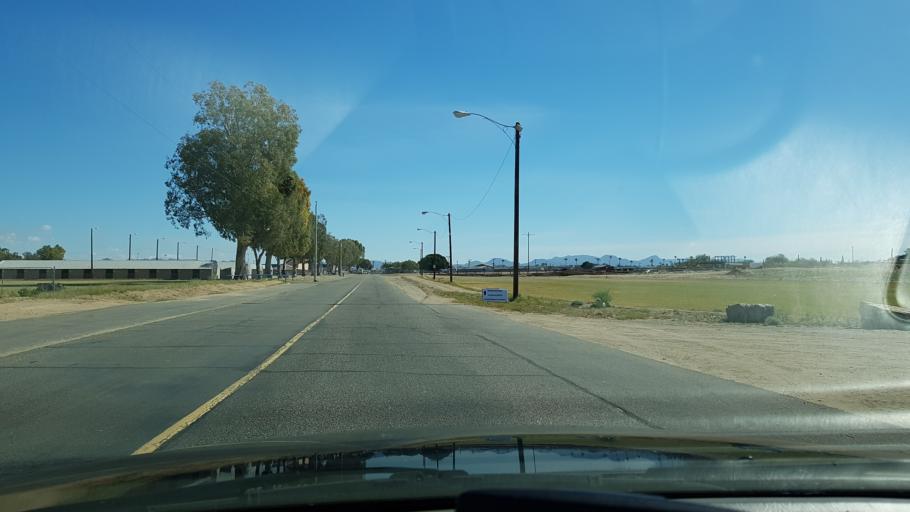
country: US
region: Arizona
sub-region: Yuma County
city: Yuma
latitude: 32.6730
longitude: -114.5976
